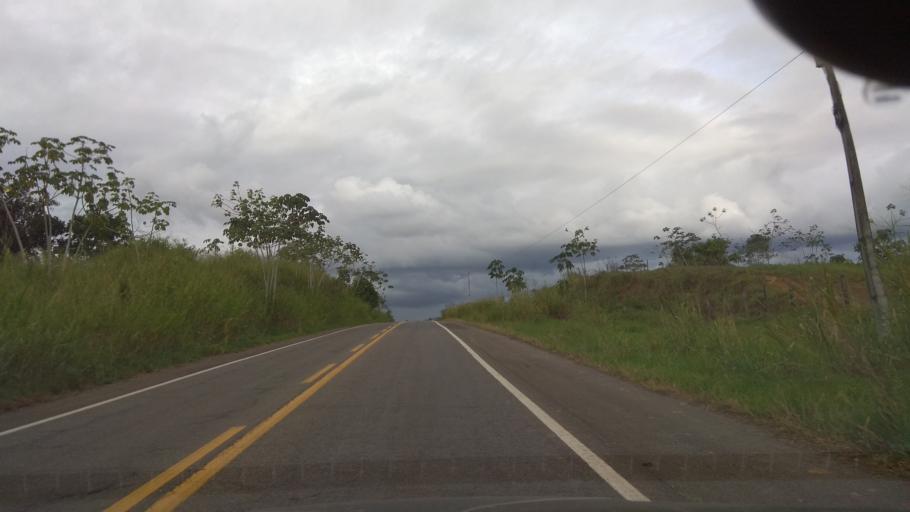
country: BR
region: Bahia
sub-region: Ipiau
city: Ipiau
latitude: -14.1949
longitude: -39.6393
